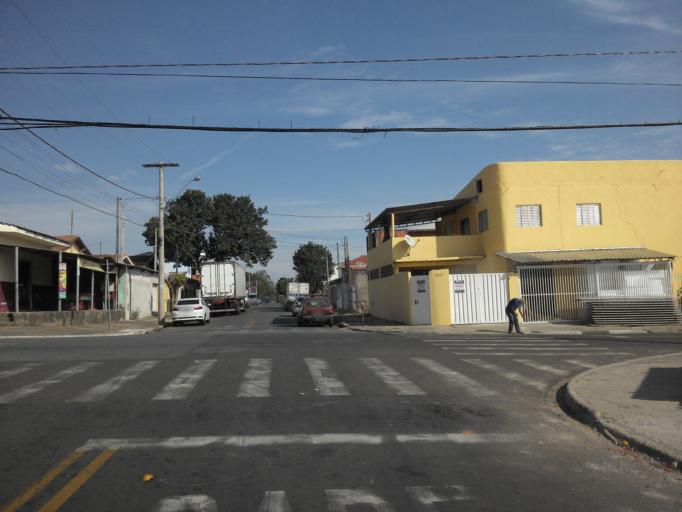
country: BR
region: Sao Paulo
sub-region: Hortolandia
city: Hortolandia
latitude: -22.8965
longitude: -47.2308
